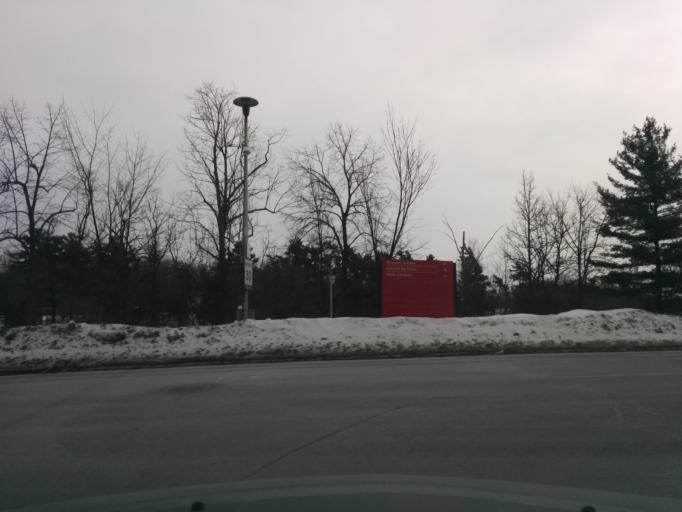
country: CA
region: Ontario
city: Ottawa
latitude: 45.3793
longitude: -75.7005
